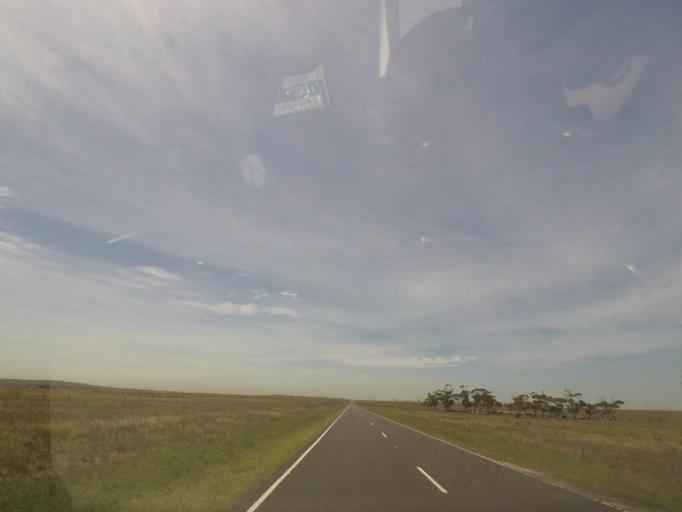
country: AU
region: Victoria
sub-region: Wyndham
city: Wyndham Vale
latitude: -37.8034
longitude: 144.4951
